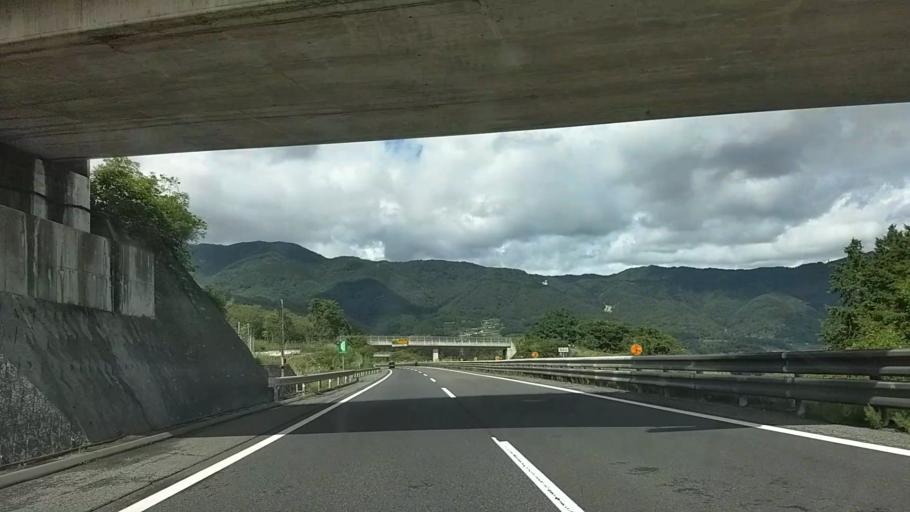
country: JP
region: Nagano
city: Nagano-shi
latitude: 36.5047
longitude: 138.0896
